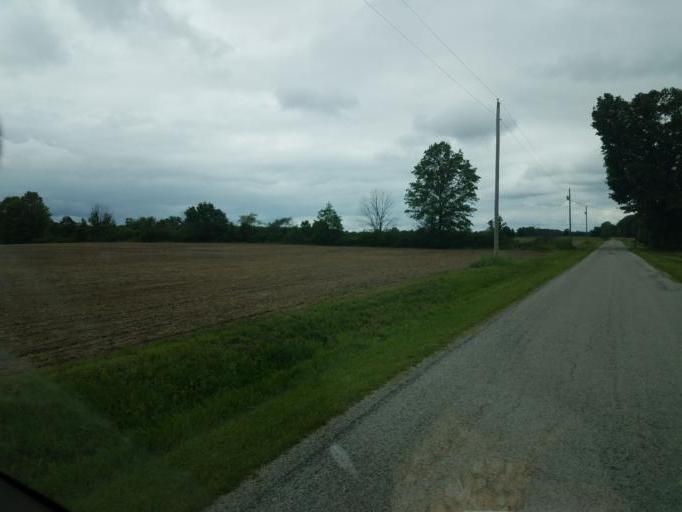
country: US
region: Ohio
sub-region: Morrow County
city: Cardington
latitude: 40.5432
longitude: -82.9709
